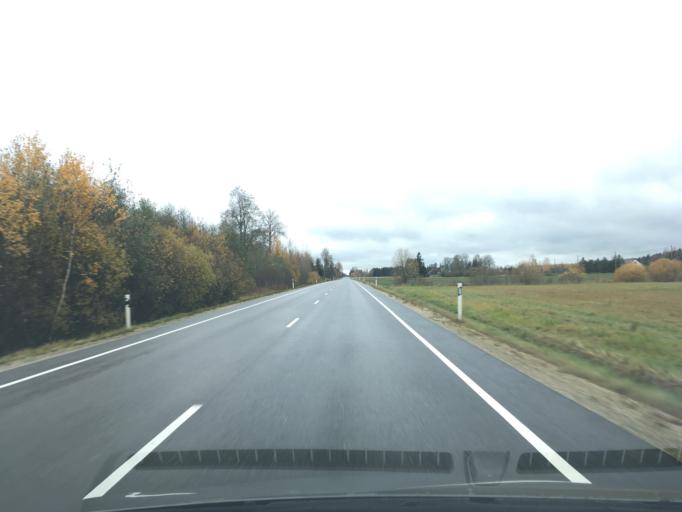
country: EE
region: Jogevamaa
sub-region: Tabivere vald
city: Tabivere
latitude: 58.4522
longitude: 26.5241
